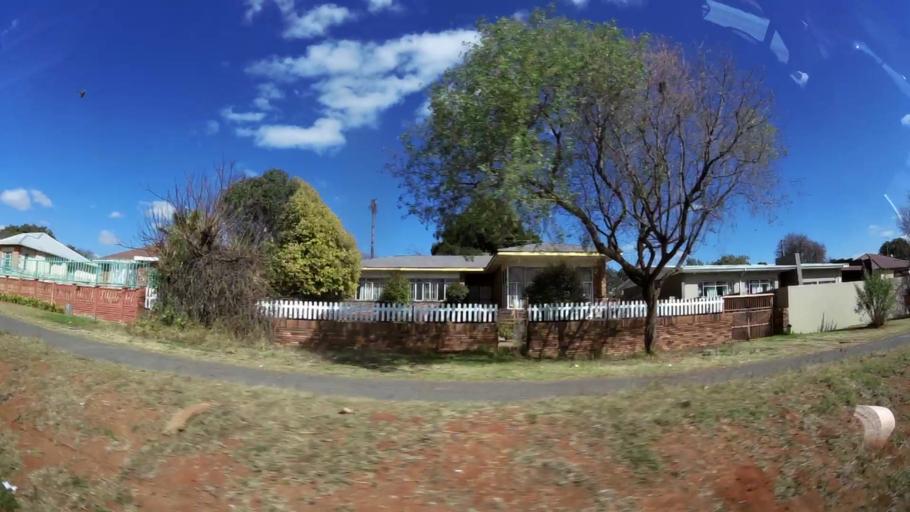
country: ZA
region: Gauteng
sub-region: West Rand District Municipality
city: Krugersdorp
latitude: -26.1094
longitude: 27.7875
